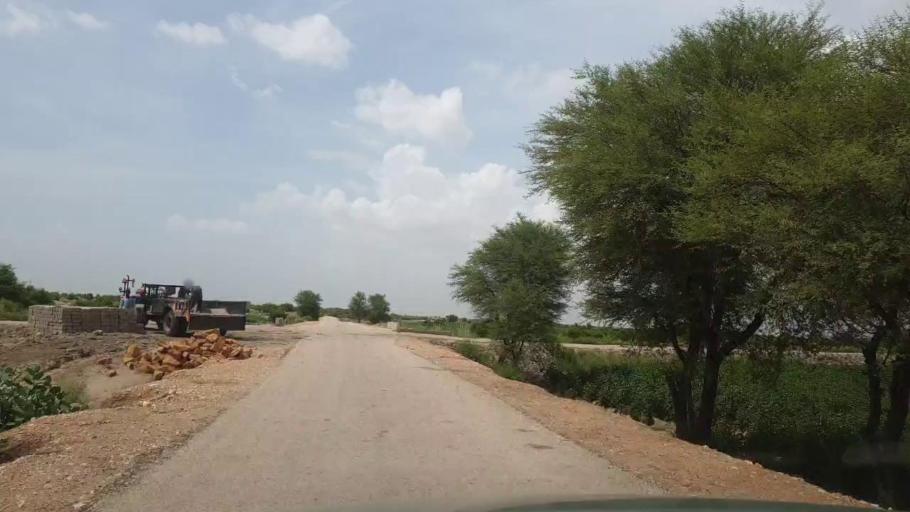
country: PK
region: Sindh
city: Kot Diji
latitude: 27.2289
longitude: 69.0893
